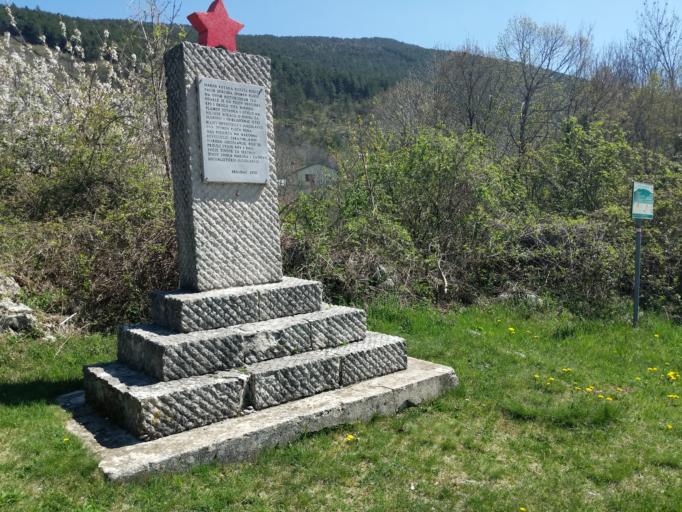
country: HR
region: Istarska
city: Lovran
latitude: 45.3811
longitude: 14.1408
